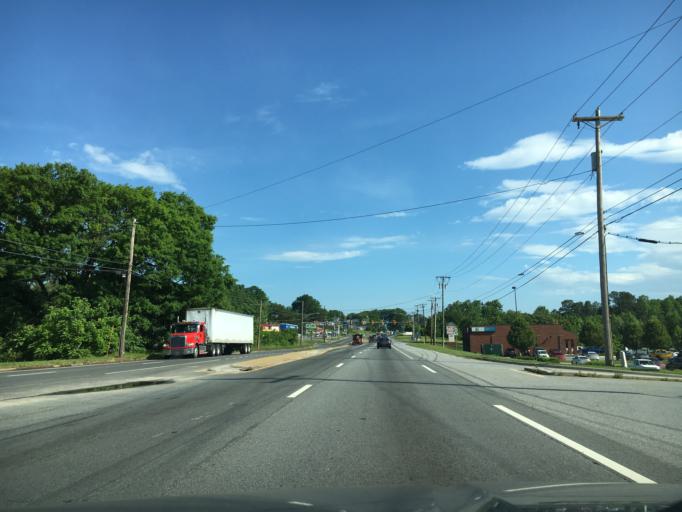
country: US
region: Virginia
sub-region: Campbell County
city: Timberlake
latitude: 37.3171
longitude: -79.1881
